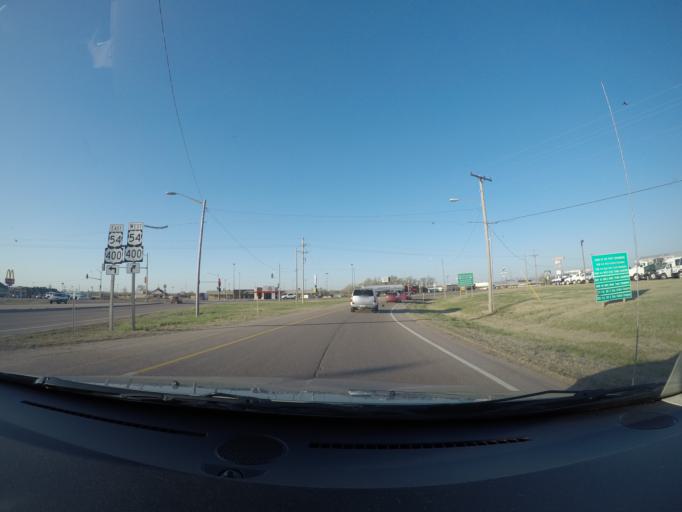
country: US
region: Kansas
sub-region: Pratt County
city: Pratt
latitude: 37.6466
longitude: -98.7168
